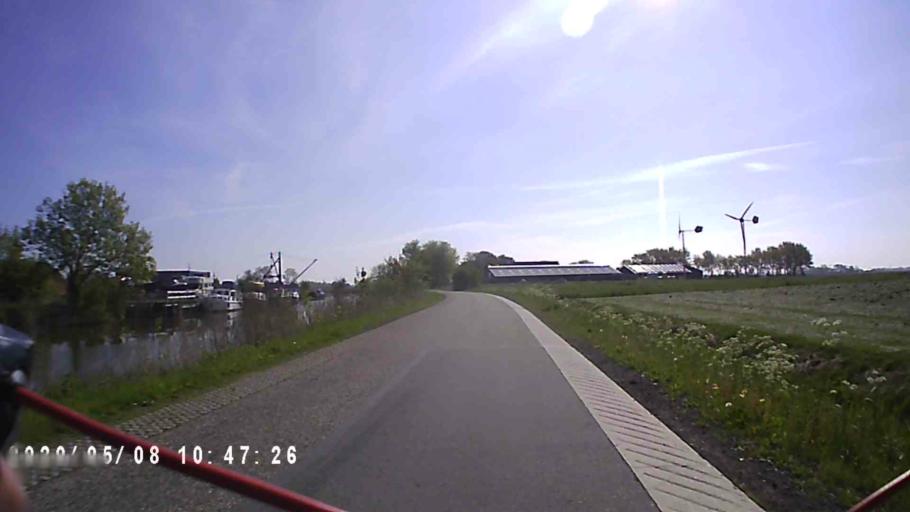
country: NL
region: Groningen
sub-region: Gemeente Winsum
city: Winsum
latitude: 53.3341
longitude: 6.5475
